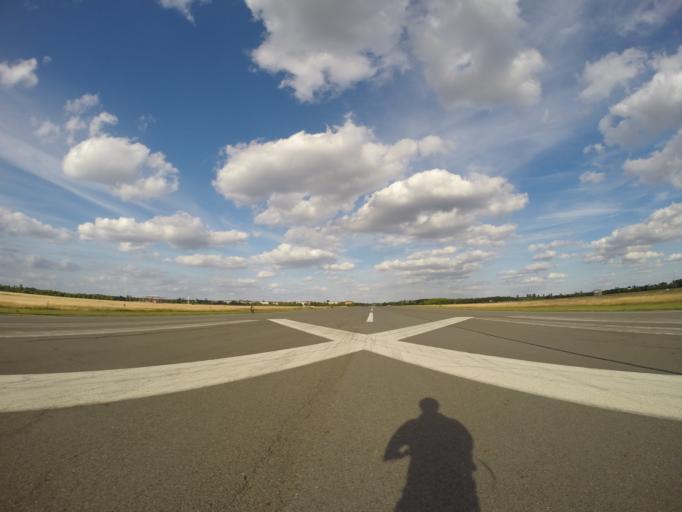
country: DE
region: Berlin
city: Tempelhof Bezirk
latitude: 52.4711
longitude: 13.4017
